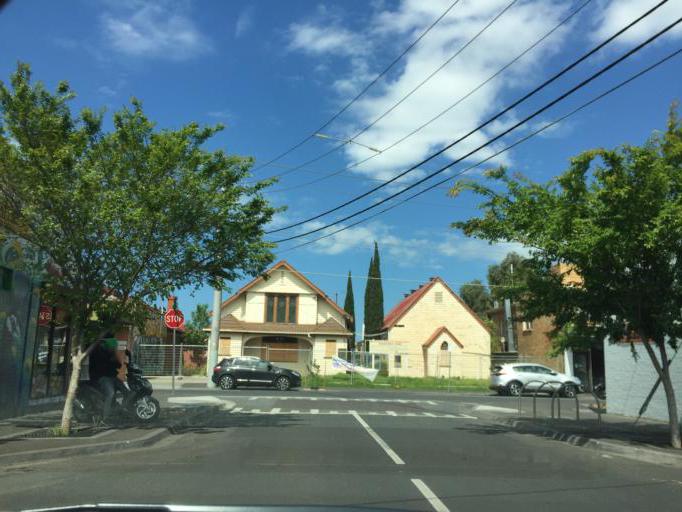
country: AU
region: Victoria
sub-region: Maribyrnong
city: West Footscray
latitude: -37.7971
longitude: 144.8770
